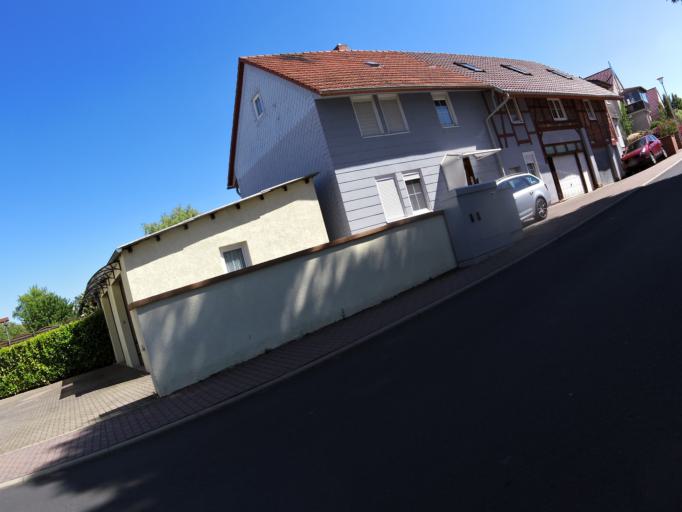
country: DE
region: Thuringia
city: Dankmarshausen
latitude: 50.9485
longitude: 10.0298
